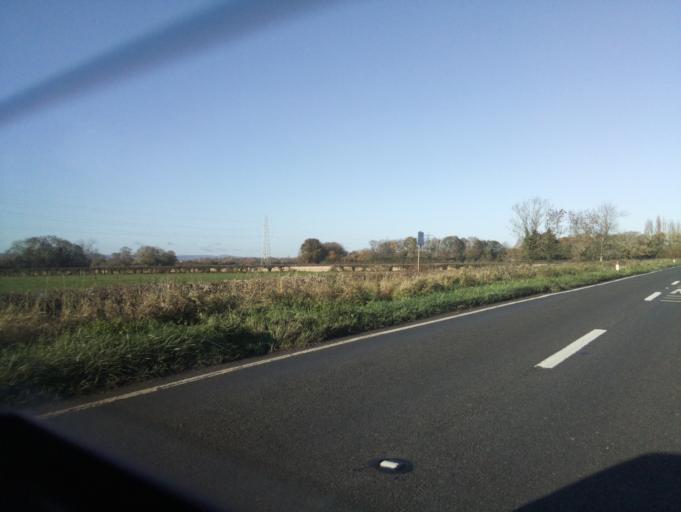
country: GB
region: England
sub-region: Somerset
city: Westonzoyland
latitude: 51.1143
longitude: -2.9622
